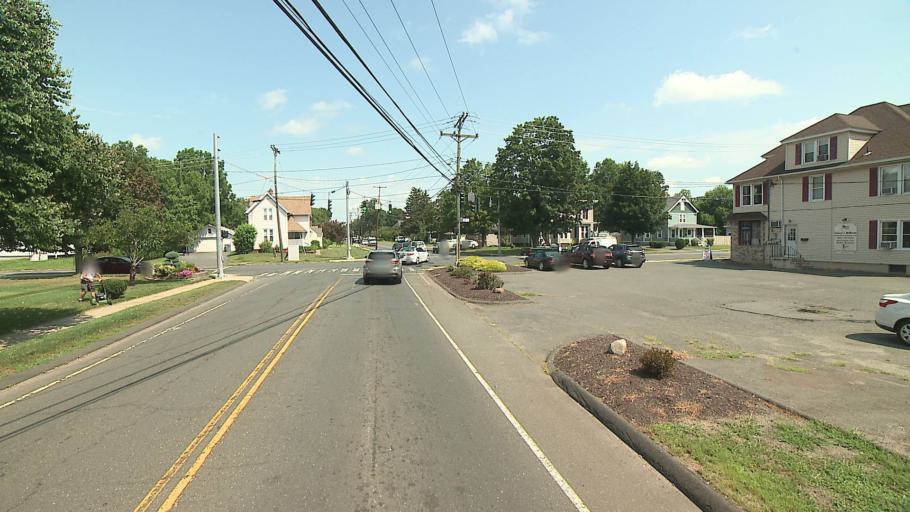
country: US
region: Connecticut
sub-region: Hartford County
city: Plainville
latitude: 41.6667
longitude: -72.8752
